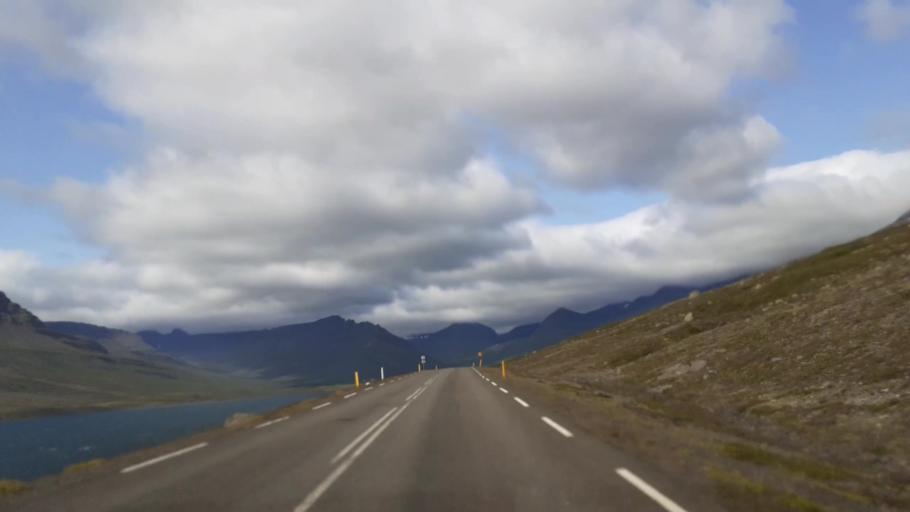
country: IS
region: East
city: Eskifjoerdur
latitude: 64.9227
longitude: -13.9746
